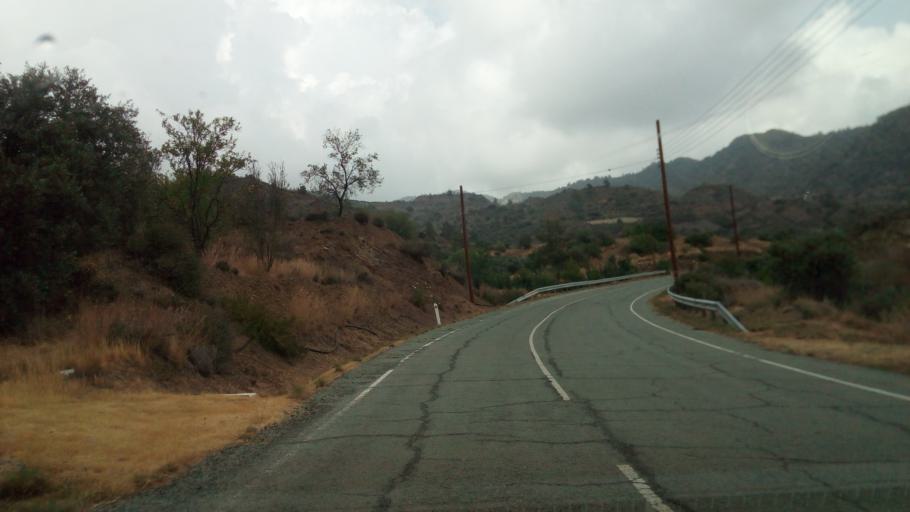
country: CY
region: Limassol
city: Parekklisha
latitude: 34.8681
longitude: 33.1897
